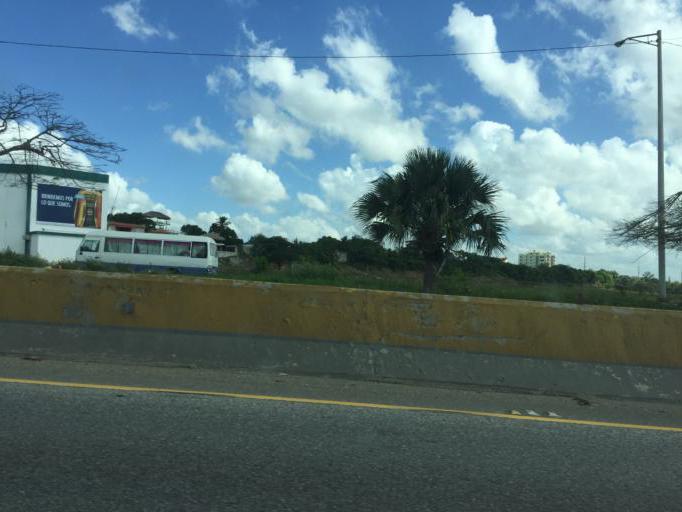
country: DO
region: Santo Domingo
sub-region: Santo Domingo
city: Santo Domingo Este
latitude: 18.4754
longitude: -69.8347
